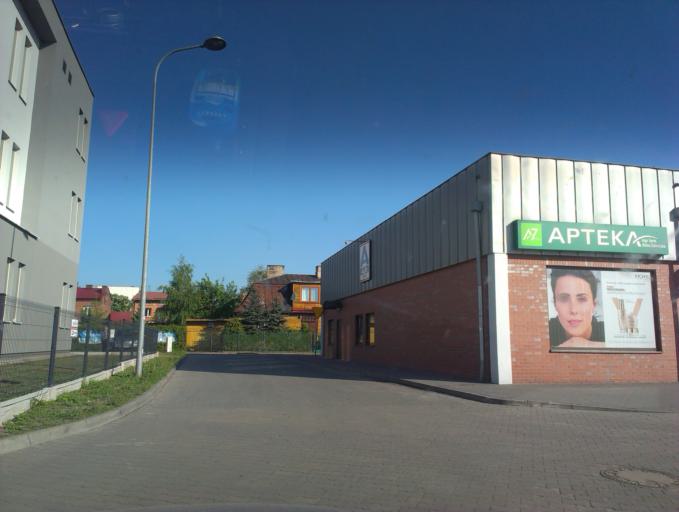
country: PL
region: Masovian Voivodeship
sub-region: Radom
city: Radom
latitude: 51.3920
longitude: 21.1474
